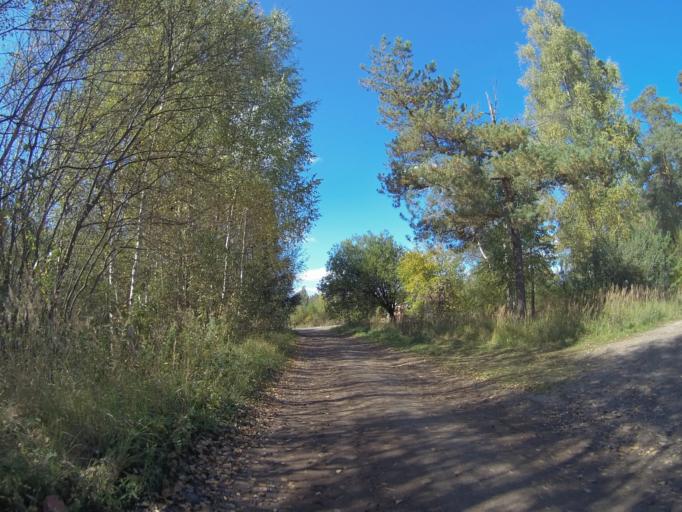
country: RU
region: Vladimir
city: Raduzhnyy
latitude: 55.9429
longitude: 40.2435
